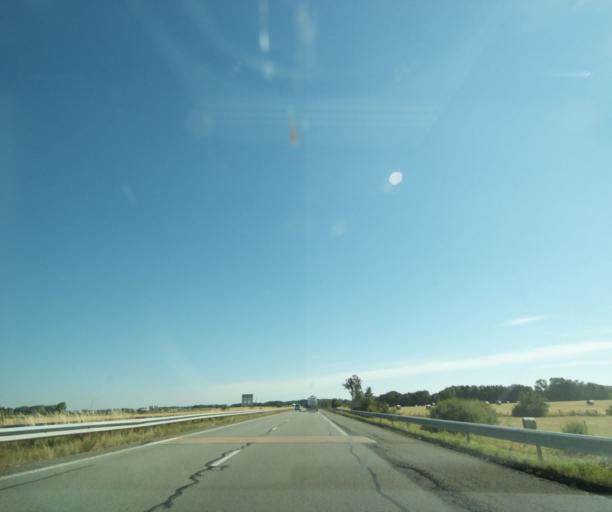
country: FR
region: Champagne-Ardenne
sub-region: Departement de la Haute-Marne
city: Avrecourt
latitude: 47.9809
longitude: 5.5027
